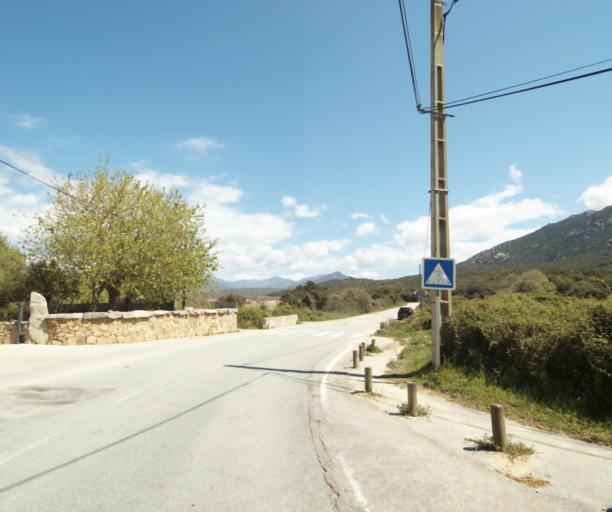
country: FR
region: Corsica
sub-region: Departement de la Corse-du-Sud
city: Propriano
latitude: 41.6448
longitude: 8.8691
